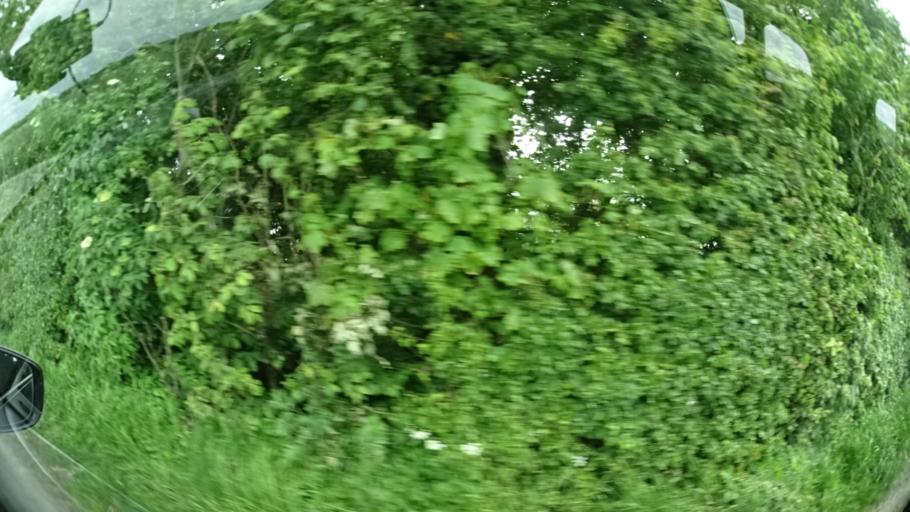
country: DK
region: Central Jutland
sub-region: Syddjurs Kommune
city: Ryomgard
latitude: 56.3971
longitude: 10.5628
